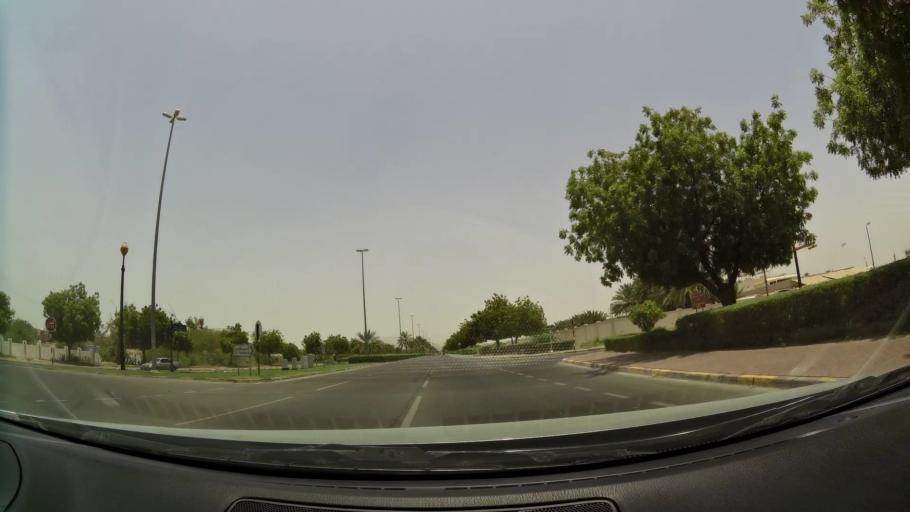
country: AE
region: Abu Dhabi
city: Al Ain
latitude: 24.2212
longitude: 55.7323
